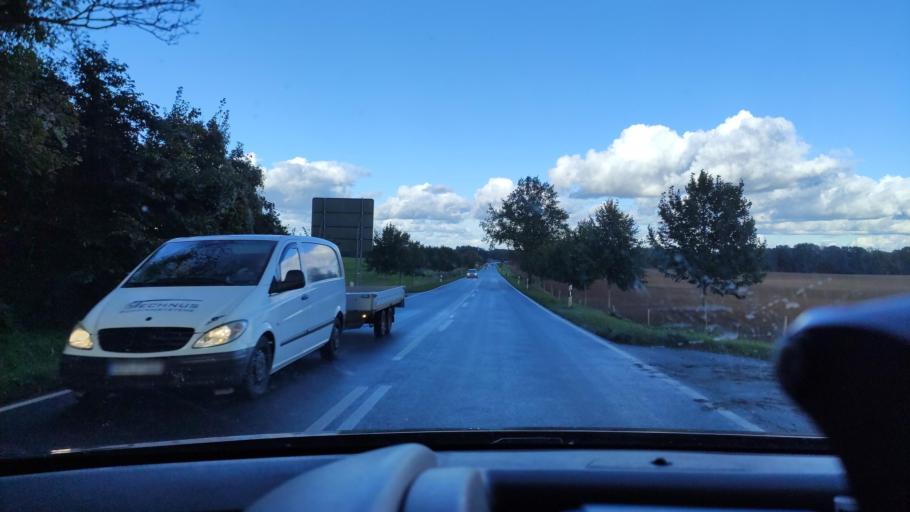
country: DE
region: Mecklenburg-Vorpommern
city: Tarnow
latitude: 53.7563
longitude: 12.0382
